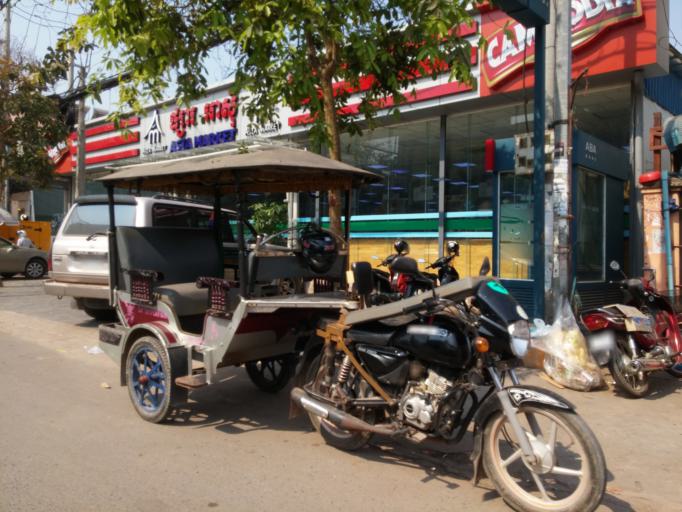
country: KH
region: Siem Reap
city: Siem Reap
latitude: 13.3578
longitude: 103.8540
